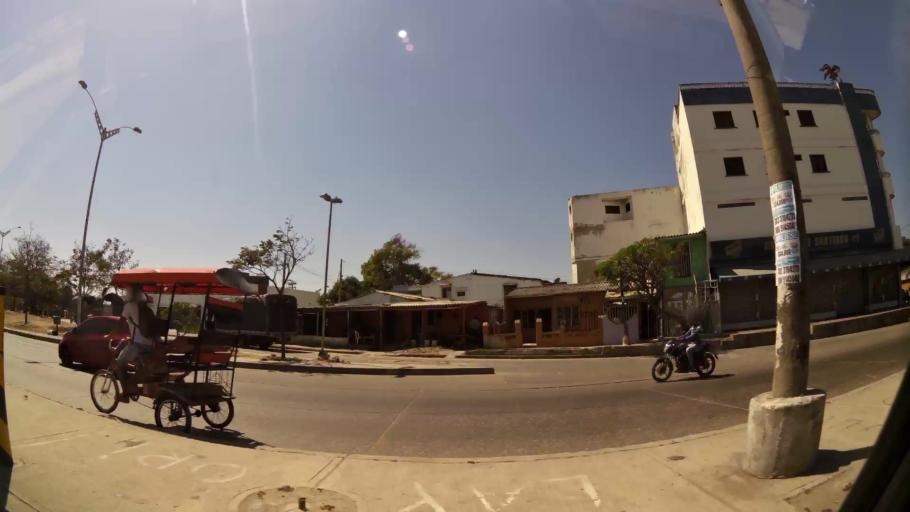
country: CO
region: Atlantico
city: Barranquilla
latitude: 10.9507
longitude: -74.7738
